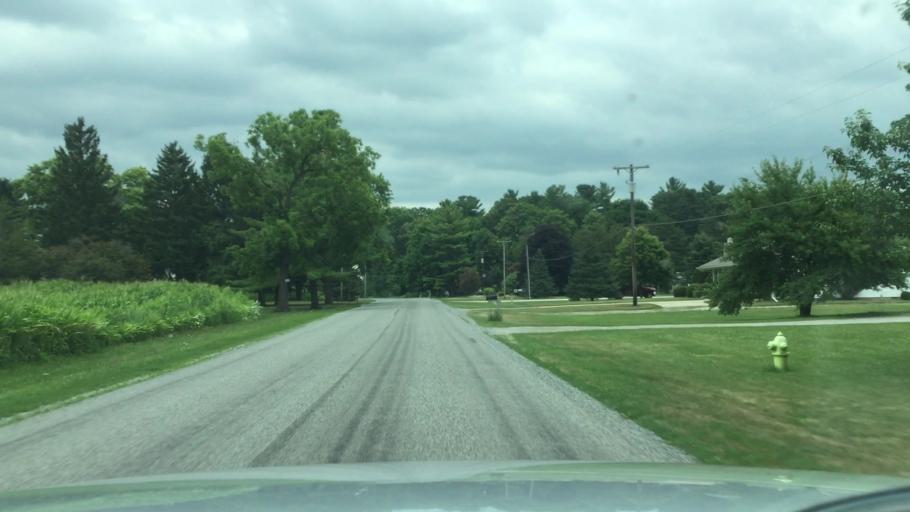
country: US
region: Michigan
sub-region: Saginaw County
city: Bridgeport
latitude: 43.3215
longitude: -83.8190
